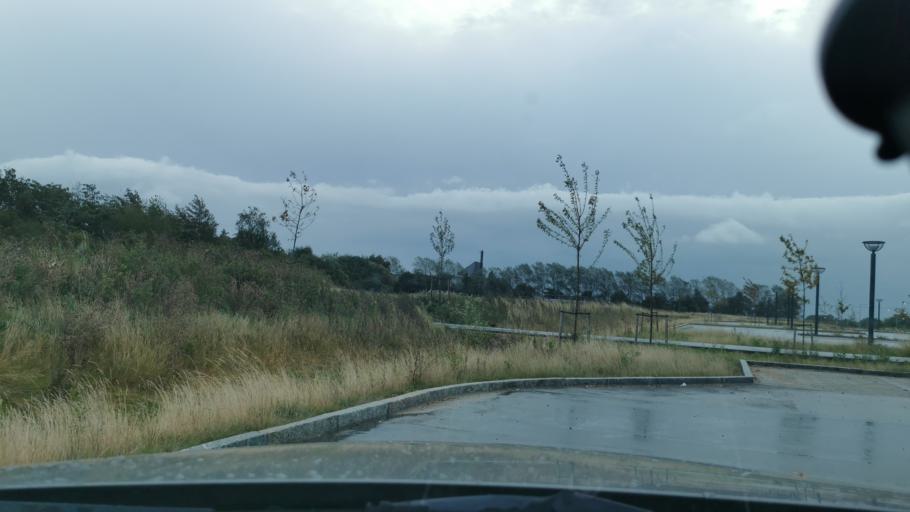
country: DK
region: Zealand
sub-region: Kalundborg Kommune
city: Kalundborg
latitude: 55.6767
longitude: 11.1242
